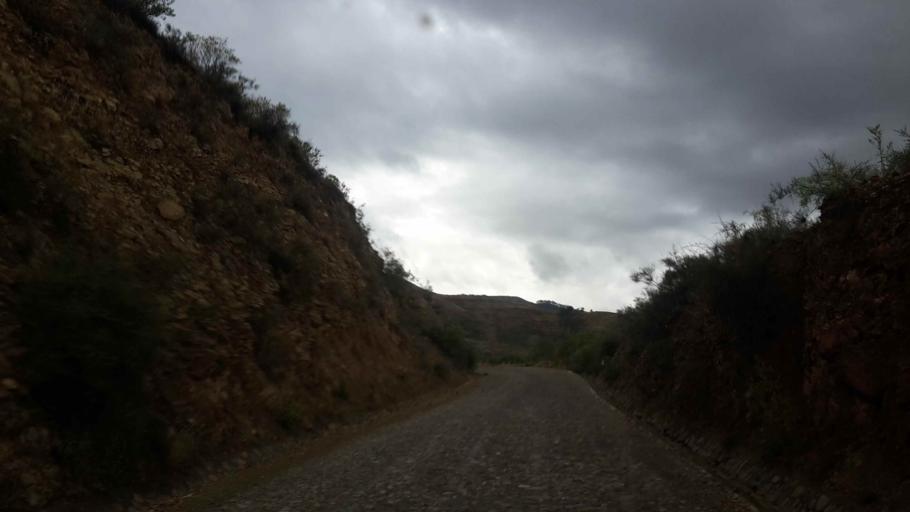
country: BO
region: Cochabamba
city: Cochabamba
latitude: -17.3681
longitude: -66.0638
